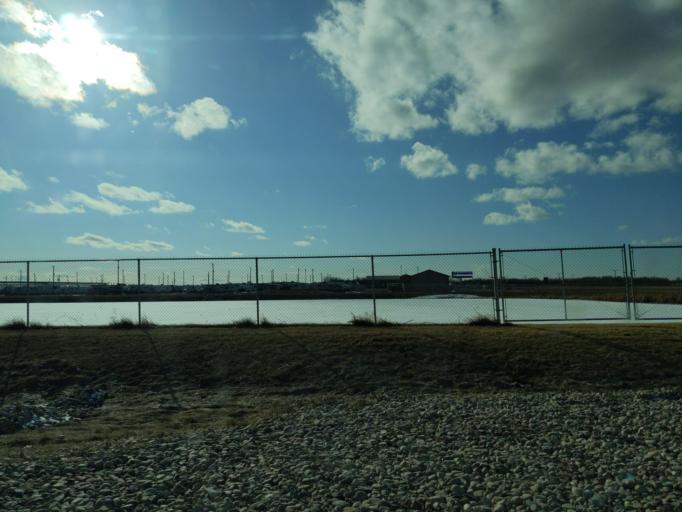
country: CA
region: Saskatchewan
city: Lloydminster
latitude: 53.2481
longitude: -109.9708
